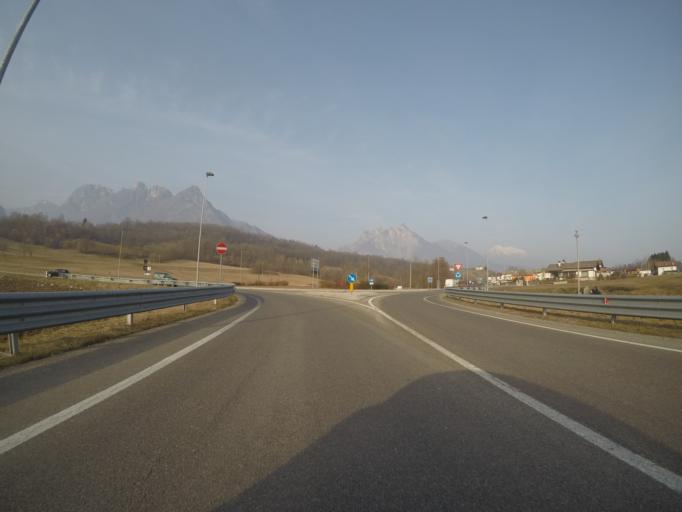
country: IT
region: Veneto
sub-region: Provincia di Belluno
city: Sospirolo
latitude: 46.1410
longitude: 12.0924
